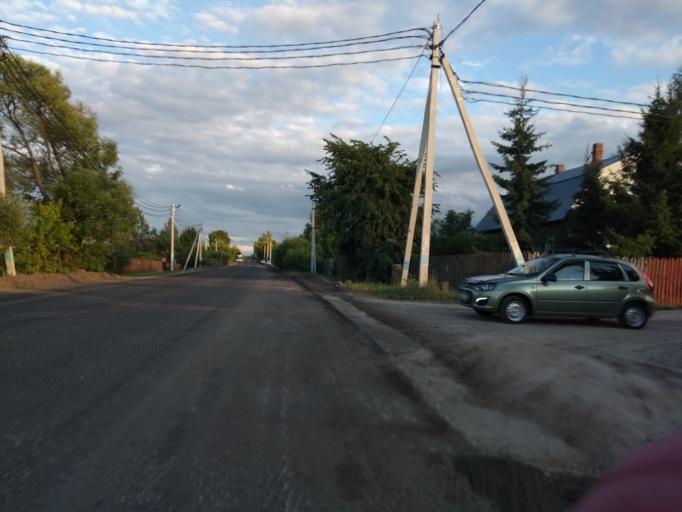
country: RU
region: Moskovskaya
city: Misheronskiy
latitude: 55.6542
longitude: 39.7526
